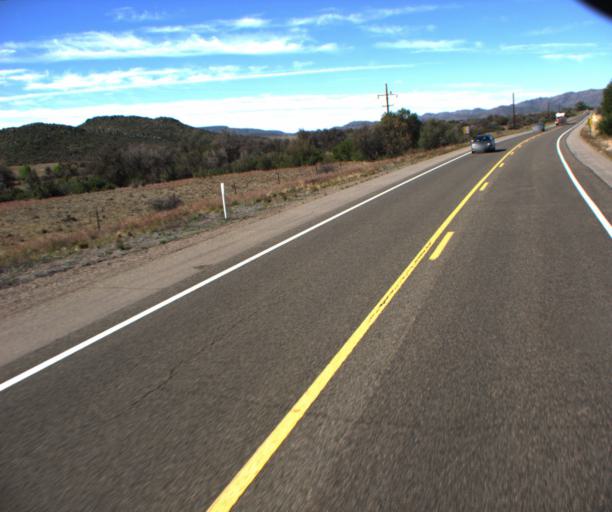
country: US
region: Arizona
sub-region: Yavapai County
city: Congress
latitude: 34.3101
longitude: -112.7106
